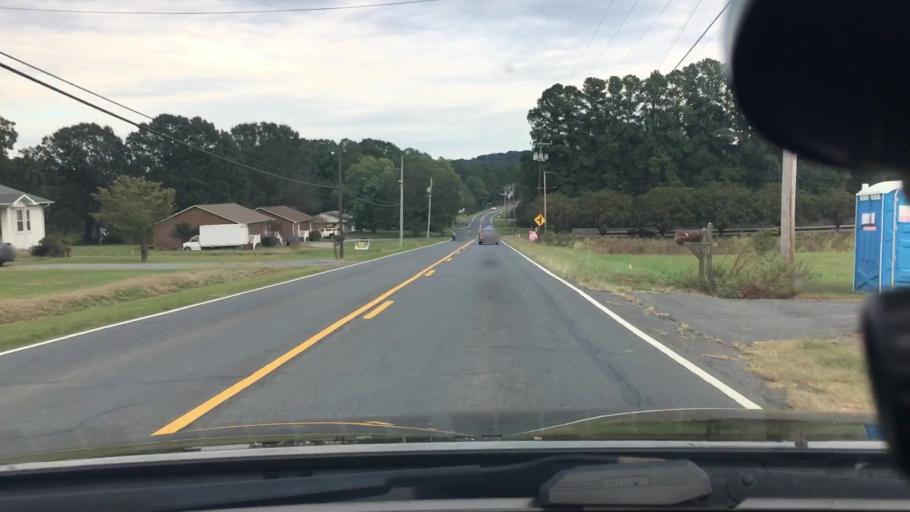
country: US
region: North Carolina
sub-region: Stanly County
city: Albemarle
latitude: 35.3445
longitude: -80.1480
